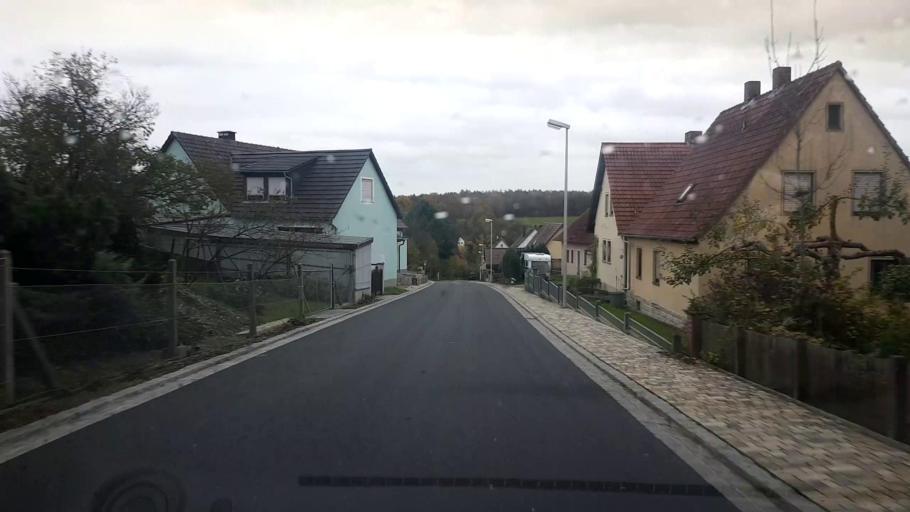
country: DE
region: Bavaria
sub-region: Upper Franconia
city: Burgwindheim
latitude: 49.8744
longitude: 10.5635
